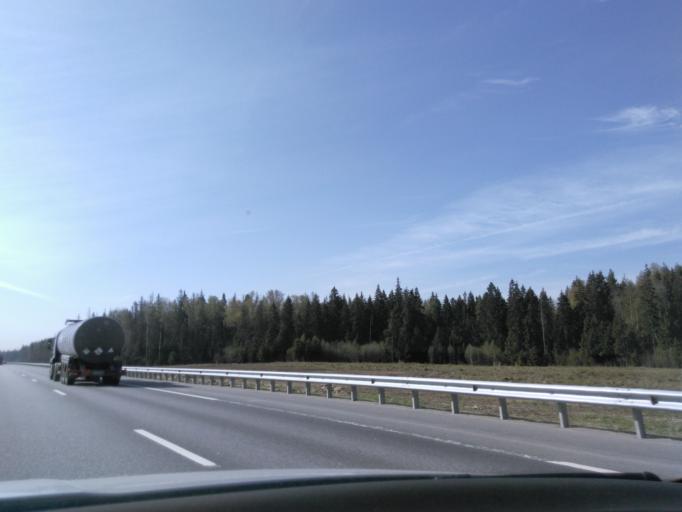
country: RU
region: Moskovskaya
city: Skhodnya
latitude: 55.9960
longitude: 37.2986
